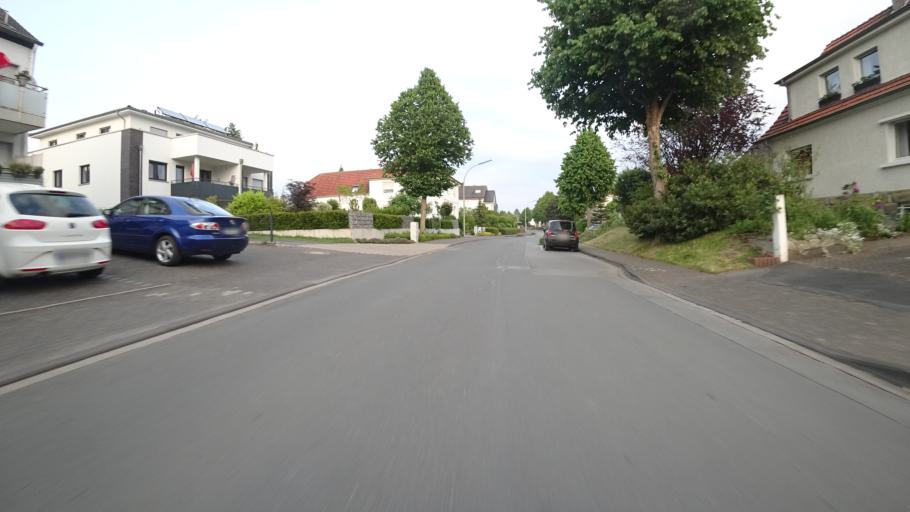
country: DE
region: North Rhine-Westphalia
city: Erwitte
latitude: 51.6357
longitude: 8.3581
